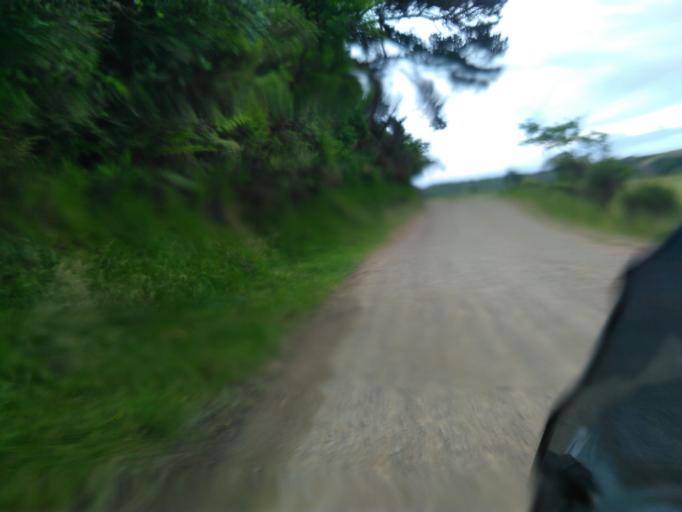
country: NZ
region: Bay of Plenty
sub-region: Opotiki District
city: Opotiki
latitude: -38.0198
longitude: 177.4336
